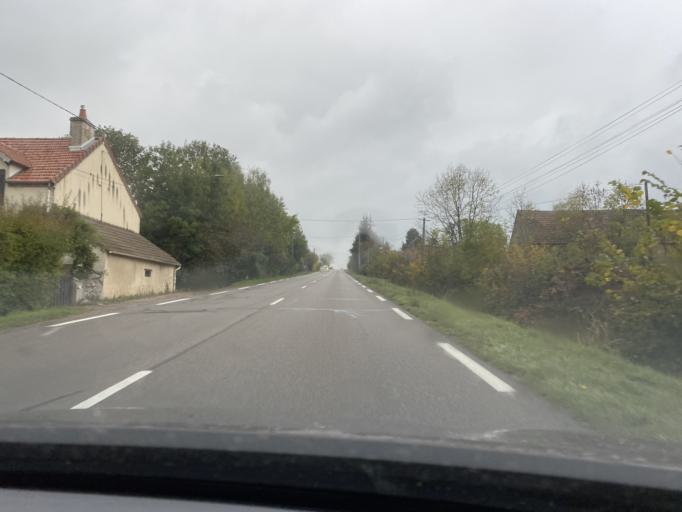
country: FR
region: Bourgogne
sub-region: Departement de la Cote-d'Or
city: Saulieu
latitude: 47.2923
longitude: 4.2195
